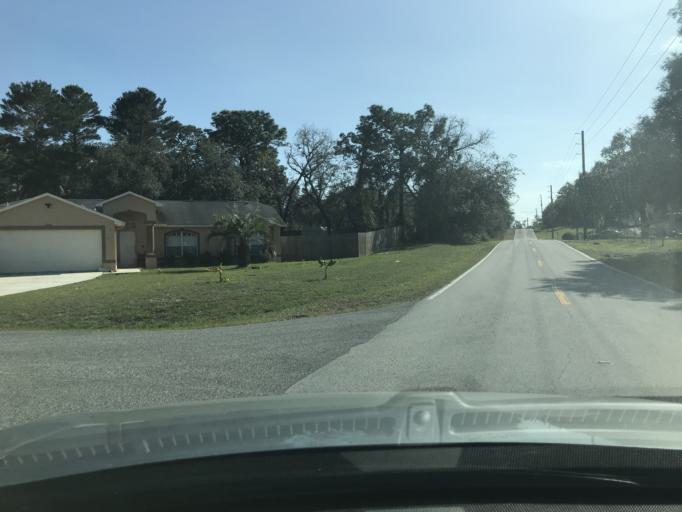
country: US
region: Florida
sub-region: Hernando County
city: North Weeki Wachee
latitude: 28.5404
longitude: -82.5473
